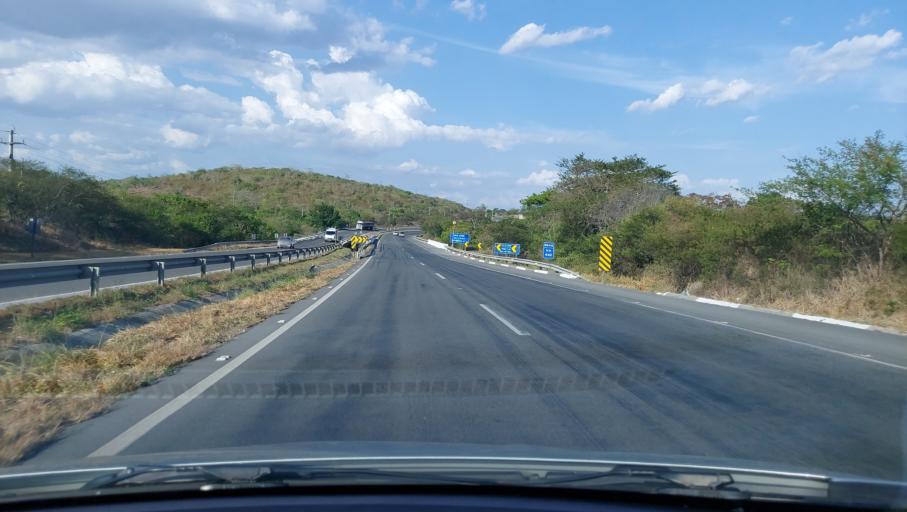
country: BR
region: Bahia
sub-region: Sao Goncalo Dos Campos
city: Sao Goncalo dos Campos
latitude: -12.3544
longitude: -39.0952
